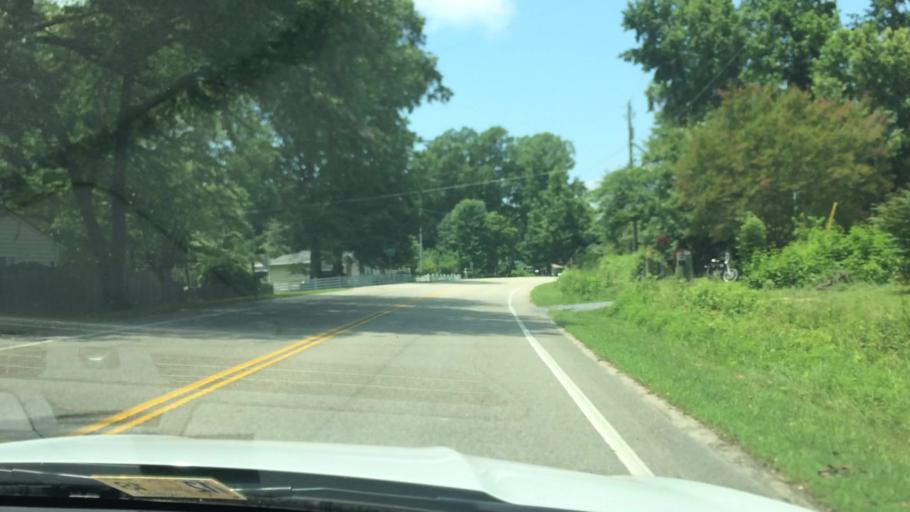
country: US
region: Virginia
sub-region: York County
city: Yorktown
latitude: 37.2041
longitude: -76.4917
